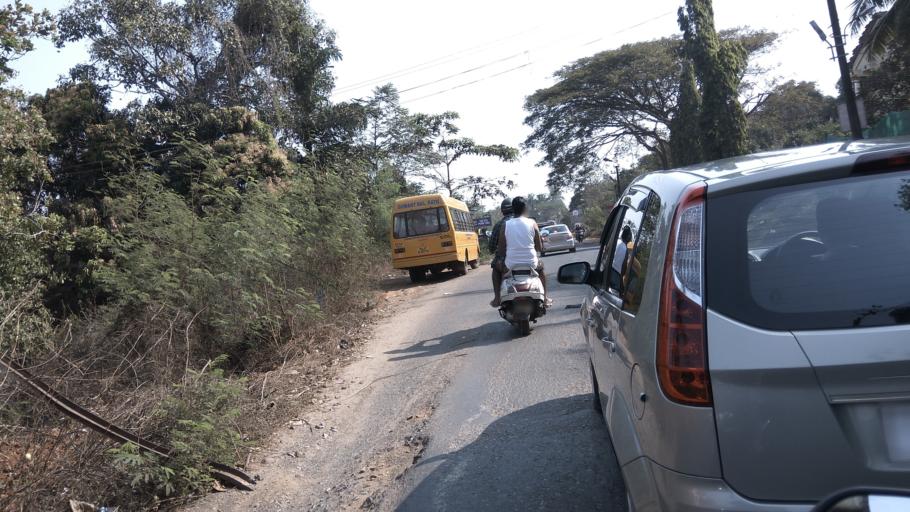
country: IN
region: Goa
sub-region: North Goa
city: Saligao
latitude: 15.5421
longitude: 73.7763
